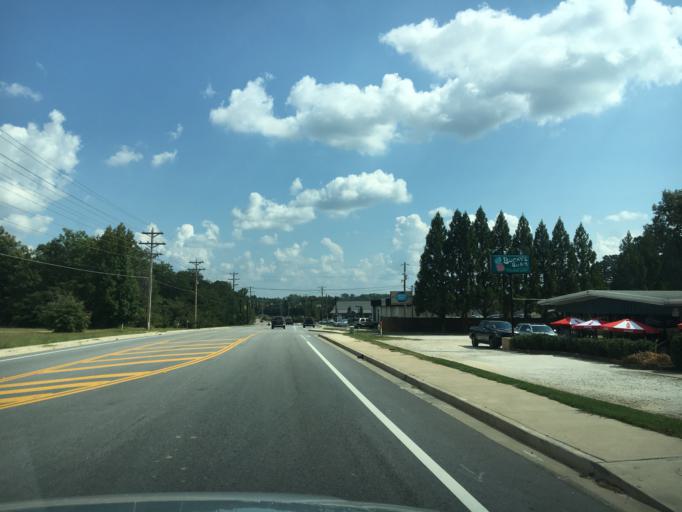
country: US
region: South Carolina
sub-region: Greenville County
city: Five Forks
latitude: 34.8341
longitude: -82.2728
